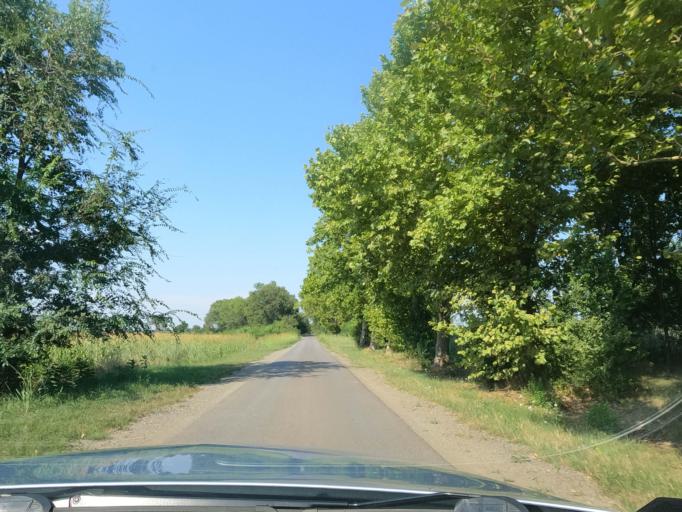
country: RS
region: Autonomna Pokrajina Vojvodina
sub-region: Juznobacki Okrug
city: Becej
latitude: 45.6621
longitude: 19.9063
